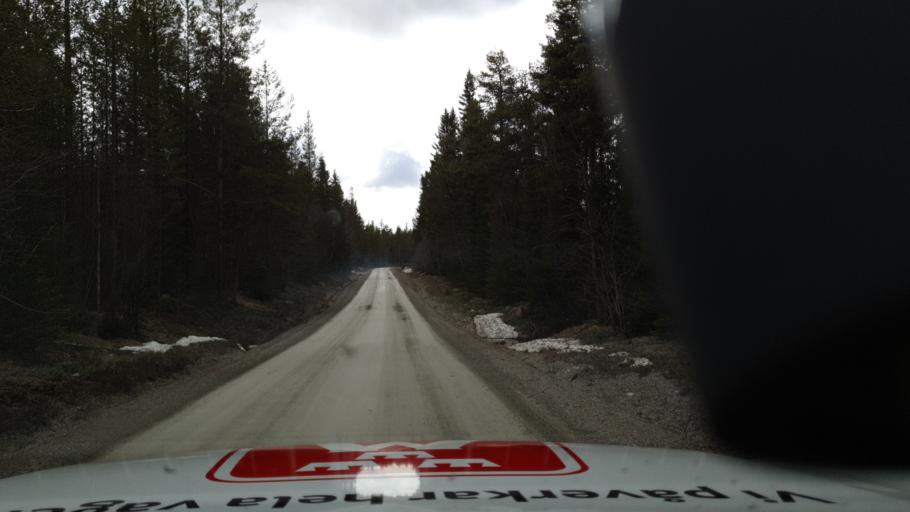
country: SE
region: Jaemtland
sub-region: Bergs Kommun
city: Hoverberg
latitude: 62.7722
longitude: 13.8279
